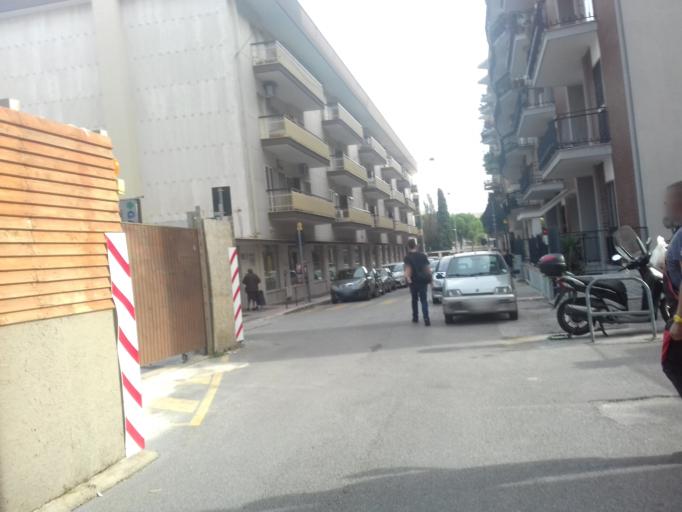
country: IT
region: Apulia
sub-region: Provincia di Bari
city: Bari
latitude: 41.1082
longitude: 16.8760
